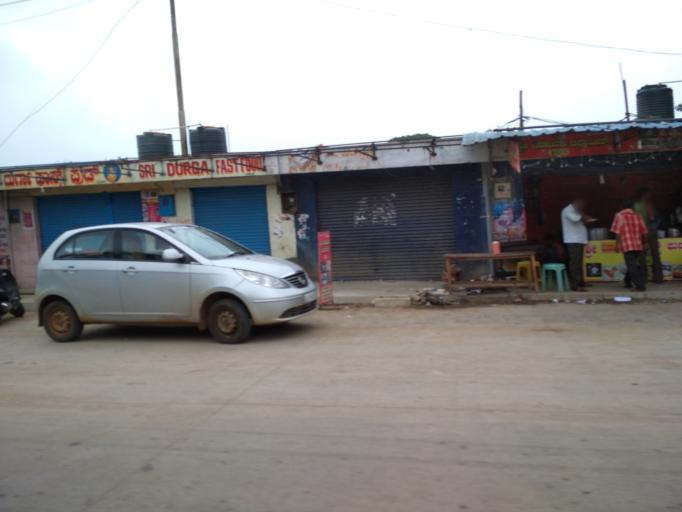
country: IN
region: Karnataka
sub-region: Mysore
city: Mysore
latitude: 12.3192
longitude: 76.6484
